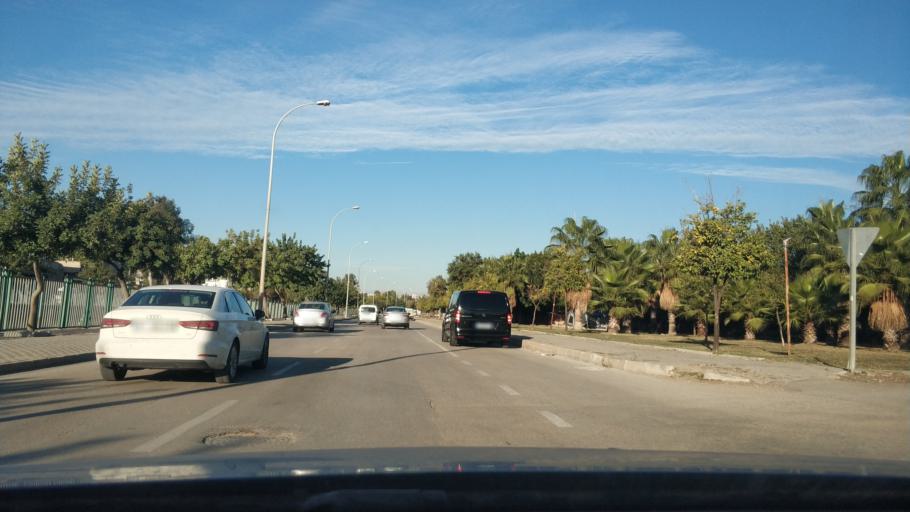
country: TR
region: Adana
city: Seyhan
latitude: 37.0110
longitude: 35.2860
